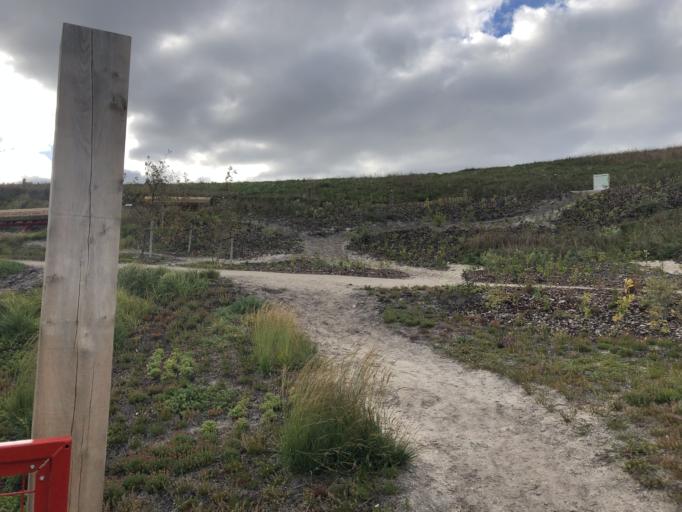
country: DK
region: Central Jutland
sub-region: Ringkobing-Skjern Kommune
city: Ringkobing
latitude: 56.1008
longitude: 8.2412
